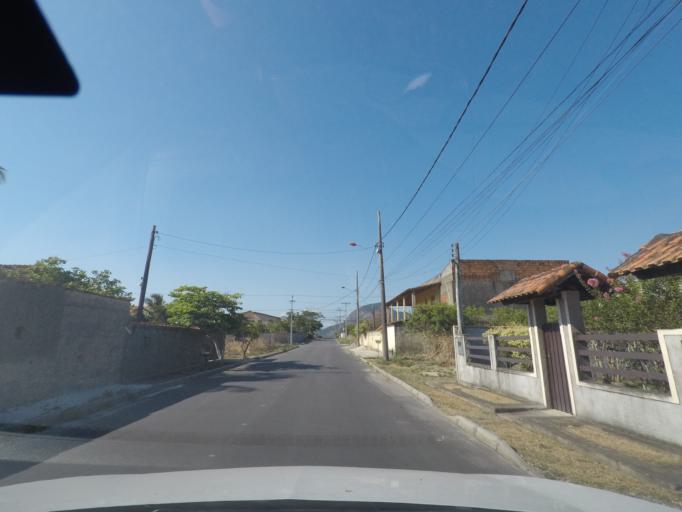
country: BR
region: Rio de Janeiro
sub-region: Marica
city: Marica
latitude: -22.9701
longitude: -42.9181
